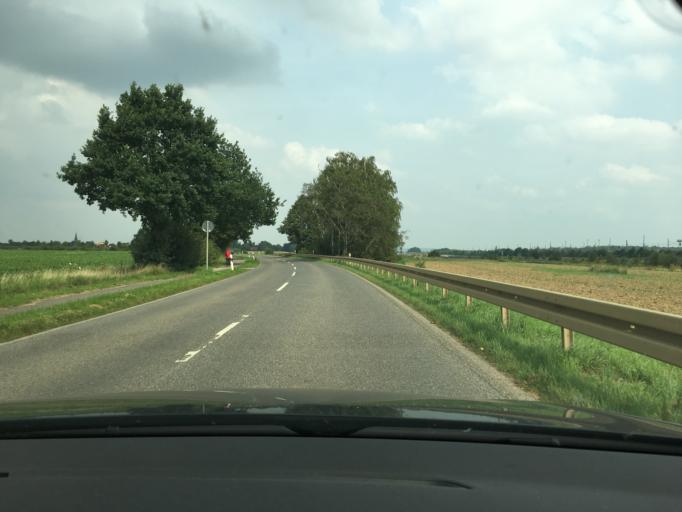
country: DE
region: North Rhine-Westphalia
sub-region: Regierungsbezirk Koln
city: Elsdorf
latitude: 50.8714
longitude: 6.5919
